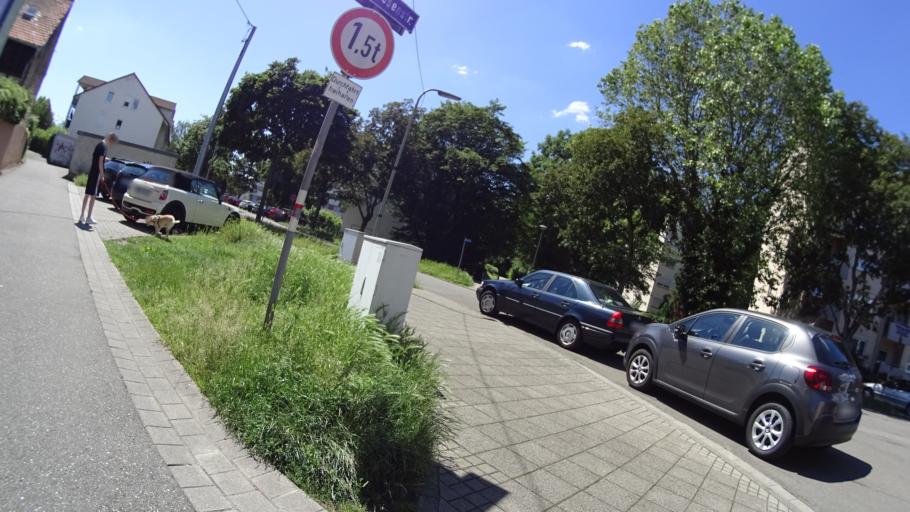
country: DE
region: Baden-Wuerttemberg
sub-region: Karlsruhe Region
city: Karlsruhe
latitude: 48.9918
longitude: 8.4591
